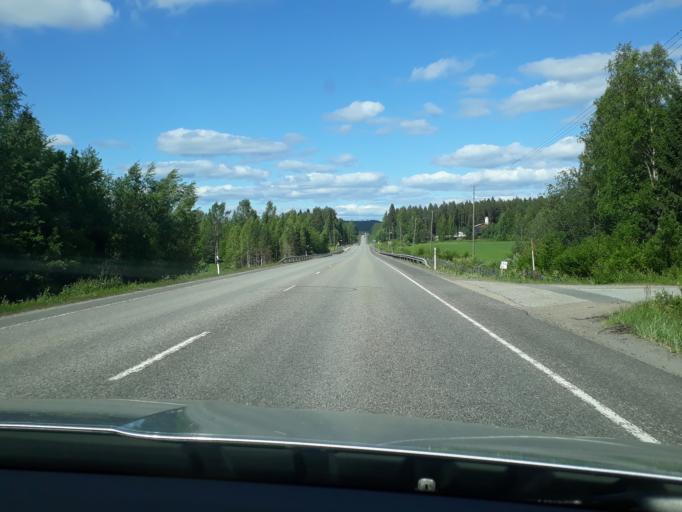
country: FI
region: Central Finland
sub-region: AEaenekoski
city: AEaenekoski
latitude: 62.6527
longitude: 25.7203
